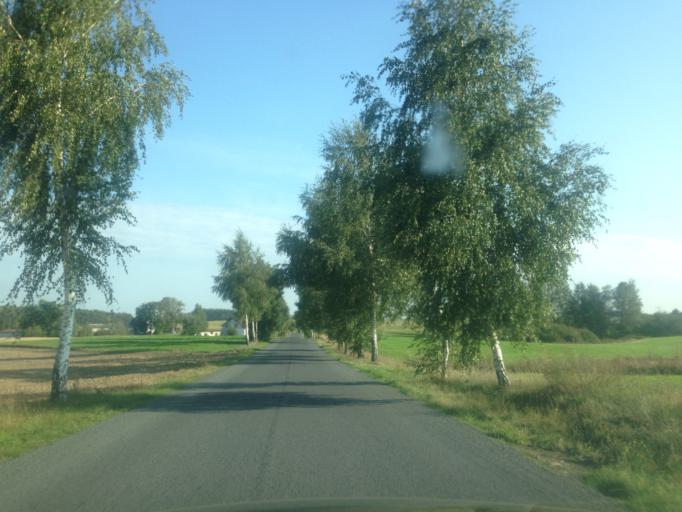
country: PL
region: Kujawsko-Pomorskie
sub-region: Powiat brodnicki
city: Brzozie
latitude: 53.3199
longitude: 19.6679
